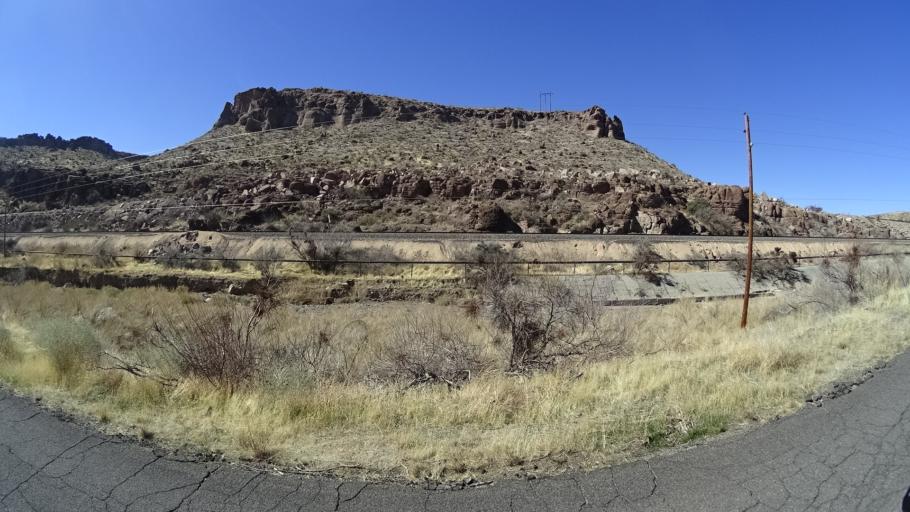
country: US
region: Arizona
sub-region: Mohave County
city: Kingman
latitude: 35.1794
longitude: -114.0627
